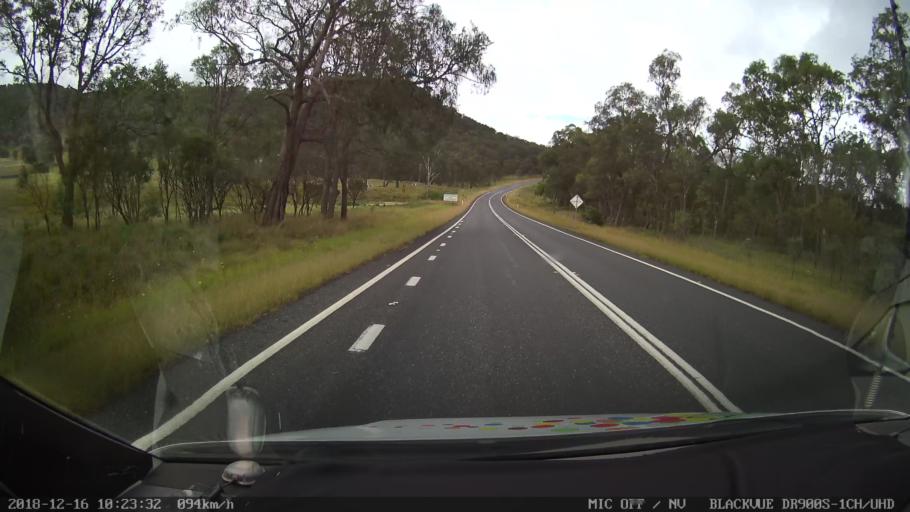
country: AU
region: New South Wales
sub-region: Tenterfield Municipality
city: Carrolls Creek
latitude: -29.1818
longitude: 152.0051
